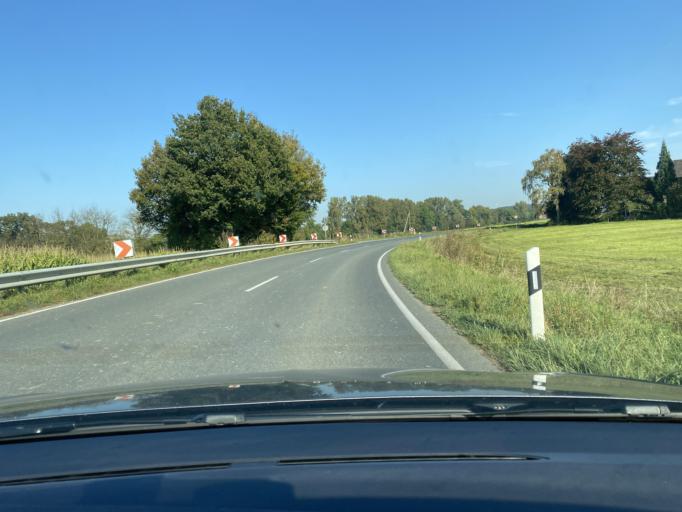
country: DE
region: North Rhine-Westphalia
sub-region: Regierungsbezirk Munster
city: Horstmar
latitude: 52.0596
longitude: 7.2772
